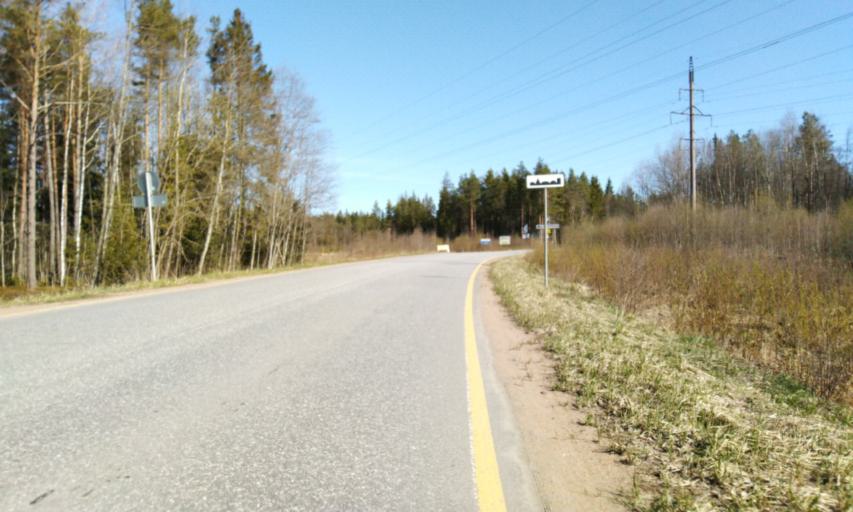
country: RU
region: Leningrad
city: Garbolovo
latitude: 60.3398
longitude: 30.4358
